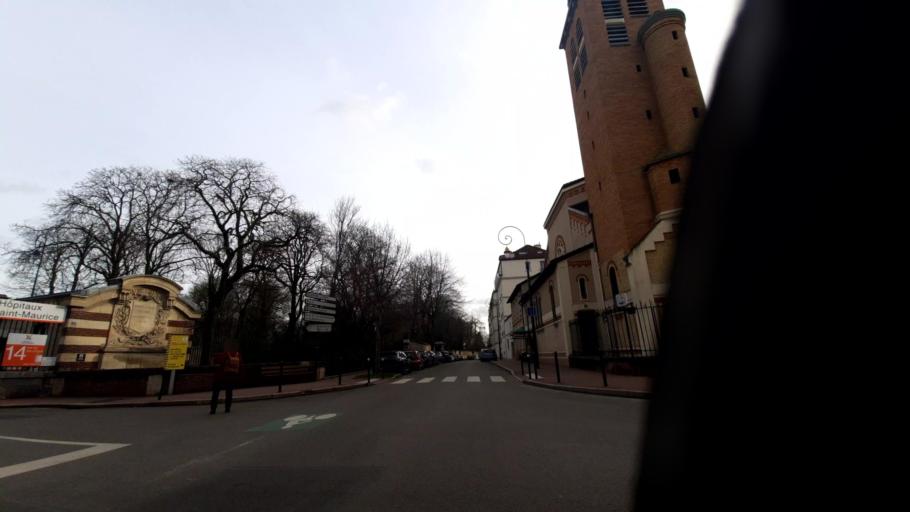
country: FR
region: Ile-de-France
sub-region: Departement du Val-de-Marne
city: Saint-Maurice
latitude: 48.8222
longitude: 2.4232
